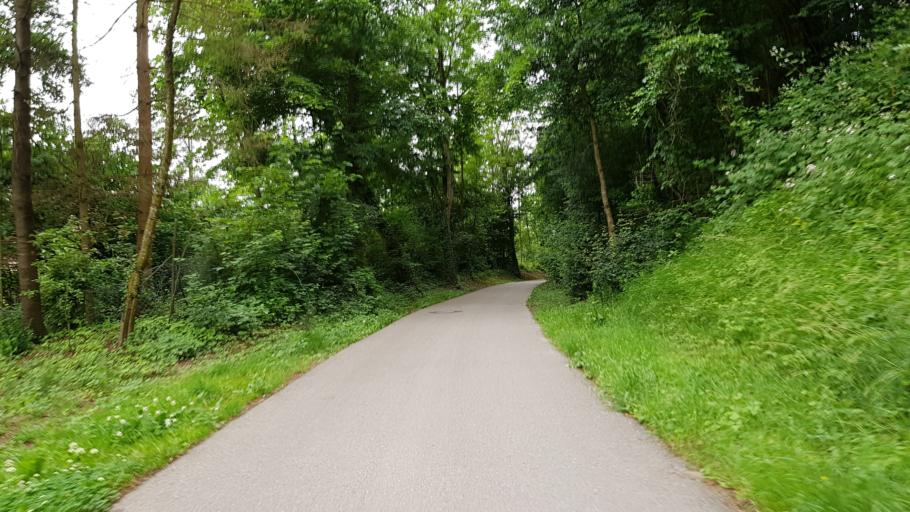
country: DE
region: Baden-Wuerttemberg
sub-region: Regierungsbezirk Stuttgart
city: Steinheim am der Murr
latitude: 48.9690
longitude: 9.2807
